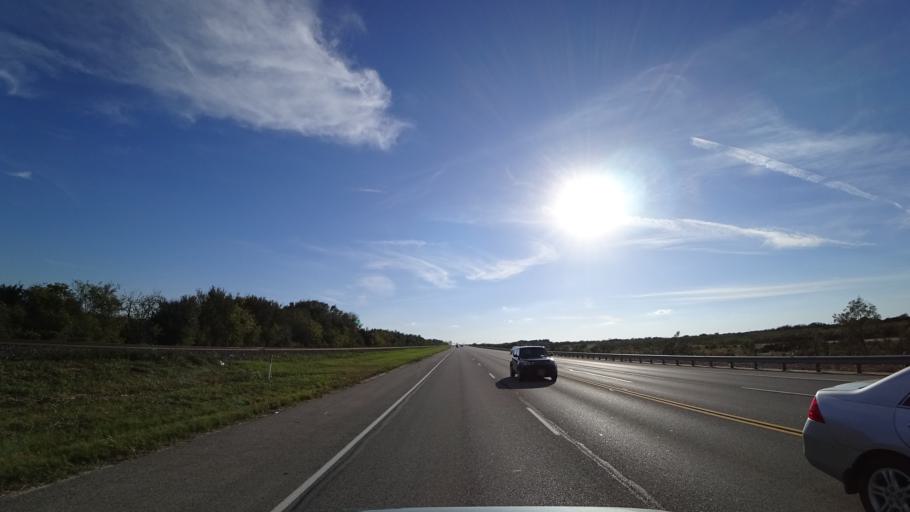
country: US
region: Texas
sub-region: Travis County
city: Wells Branch
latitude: 30.4703
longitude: -97.7099
